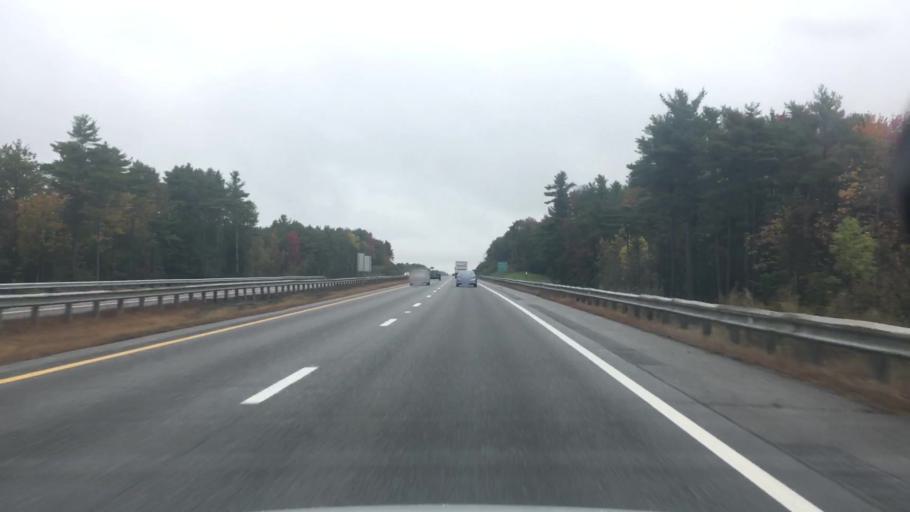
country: US
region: Maine
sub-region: Kennebec County
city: Gardiner
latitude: 44.2390
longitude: -69.8077
